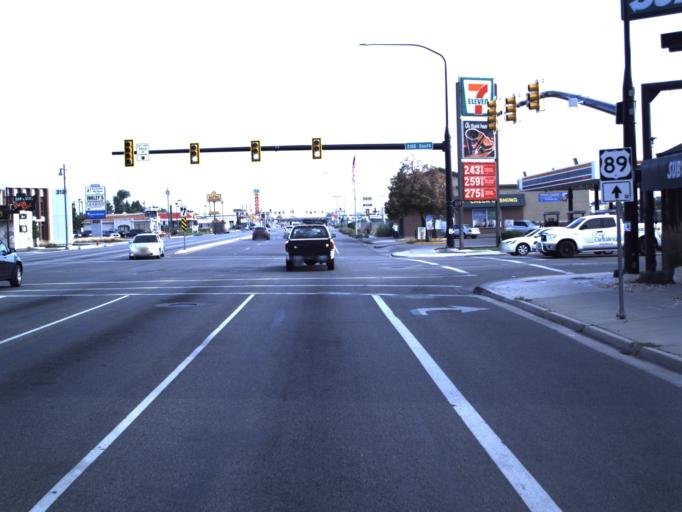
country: US
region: Utah
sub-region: Salt Lake County
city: South Salt Lake
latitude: 40.7259
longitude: -111.8884
